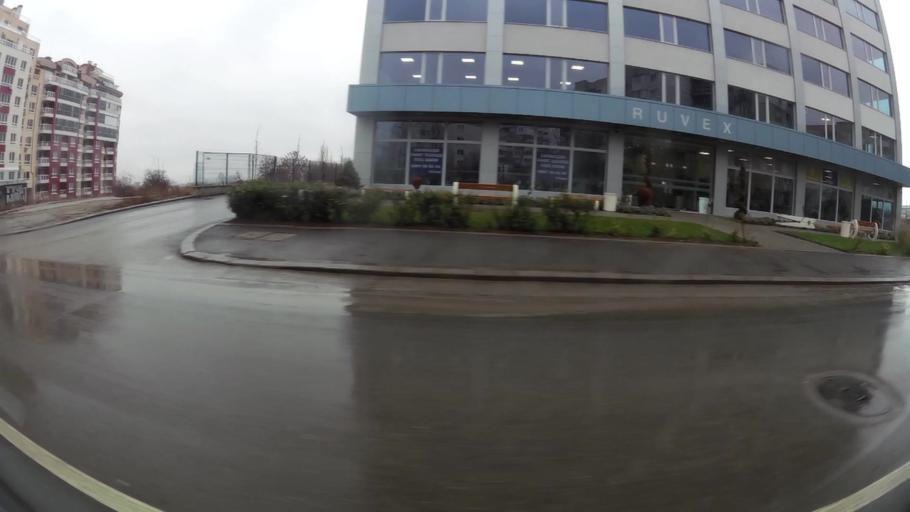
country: BG
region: Sofia-Capital
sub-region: Stolichna Obshtina
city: Sofia
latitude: 42.6294
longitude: 23.3826
